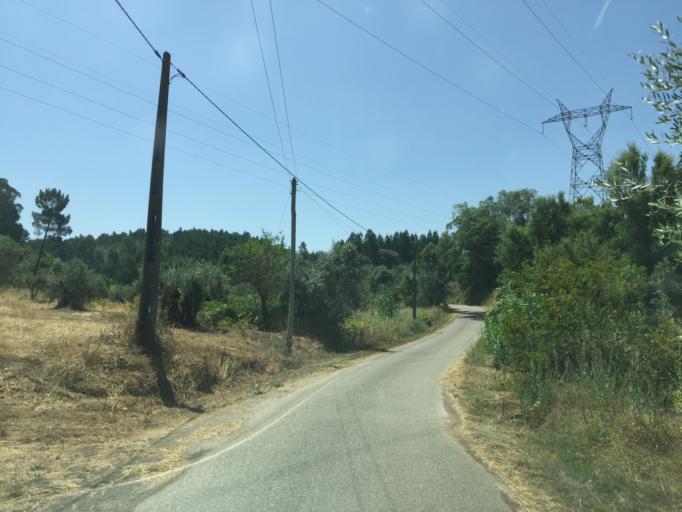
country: PT
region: Santarem
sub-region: Ferreira do Zezere
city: Ferreira do Zezere
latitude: 39.6531
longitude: -8.3025
